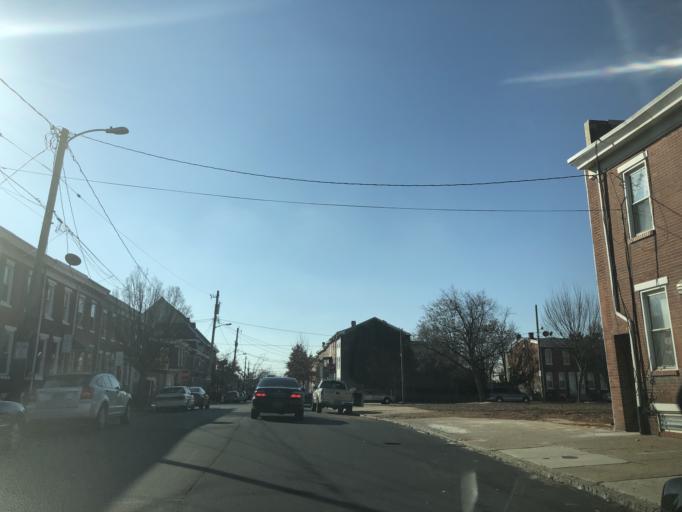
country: US
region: Delaware
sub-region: New Castle County
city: Wilmington
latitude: 39.7409
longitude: -75.5631
